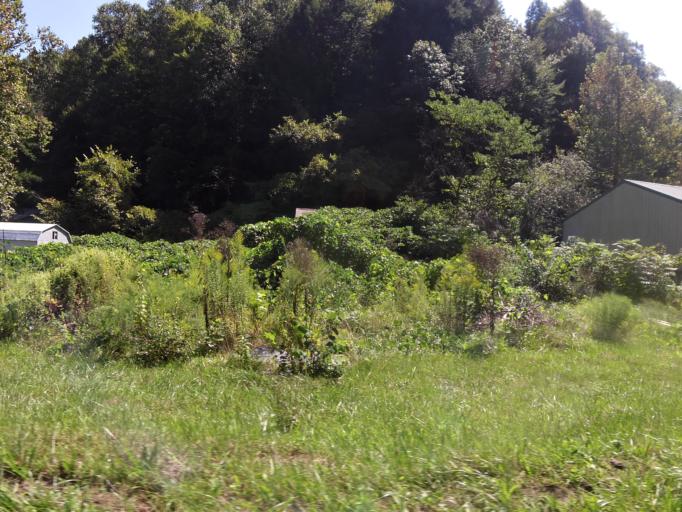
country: US
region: Kentucky
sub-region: Leslie County
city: Hyden
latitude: 37.1374
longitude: -83.4424
